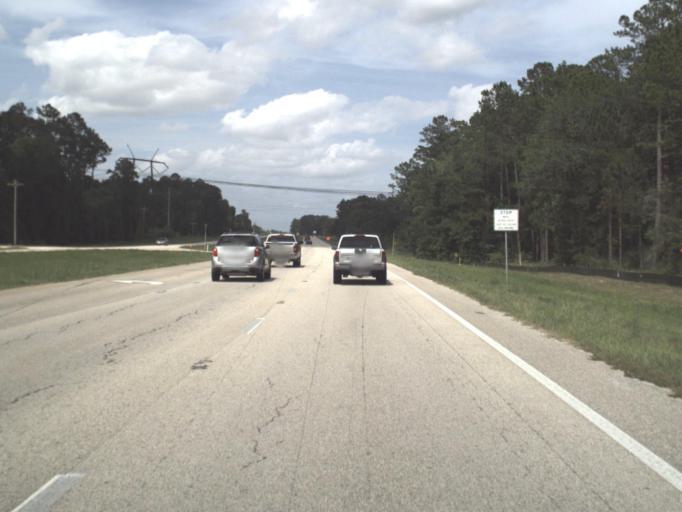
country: US
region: Florida
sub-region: Clay County
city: Middleburg
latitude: 30.0954
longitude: -81.8429
